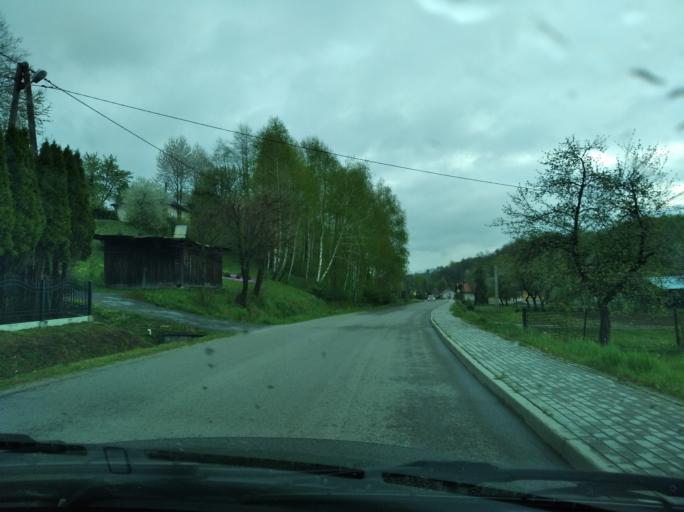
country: PL
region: Subcarpathian Voivodeship
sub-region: Powiat rzeszowski
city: Lecka
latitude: 49.8700
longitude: 22.0346
